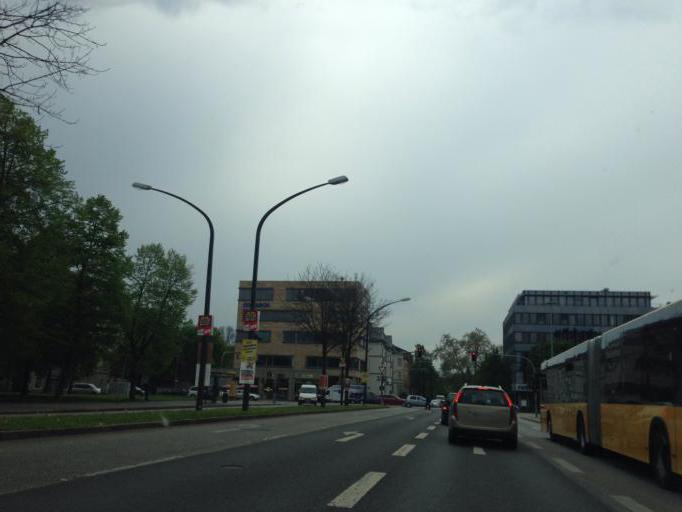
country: DE
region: Saxony
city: Dresden
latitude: 51.0376
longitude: 13.7165
